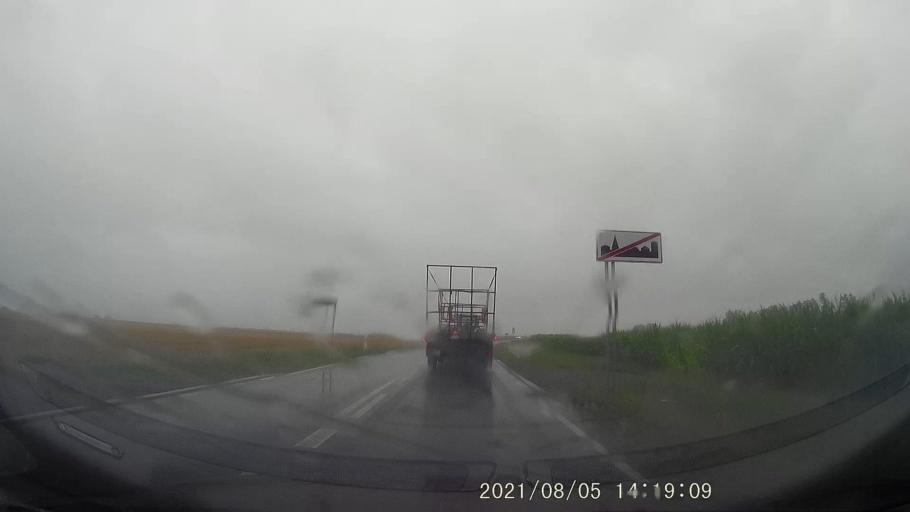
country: PL
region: Opole Voivodeship
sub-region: Powiat prudnicki
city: Biala
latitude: 50.4658
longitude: 17.6884
